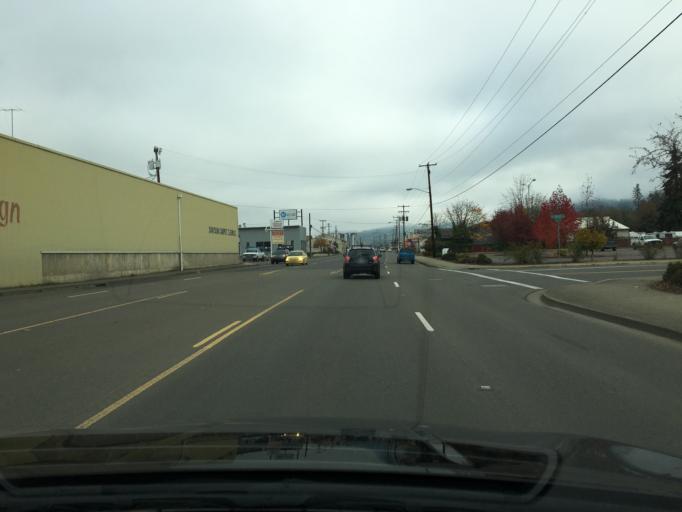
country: US
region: Oregon
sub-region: Douglas County
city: Roseburg
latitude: 43.2136
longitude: -123.3404
